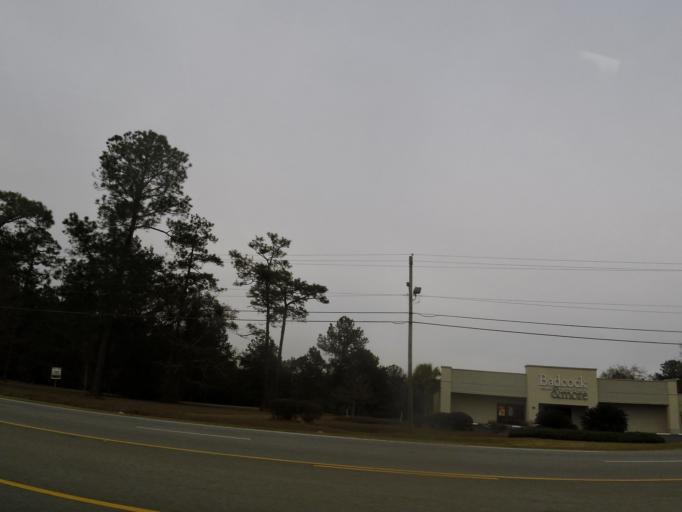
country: US
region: Georgia
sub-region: Grady County
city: Cairo
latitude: 30.8768
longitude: -84.1685
